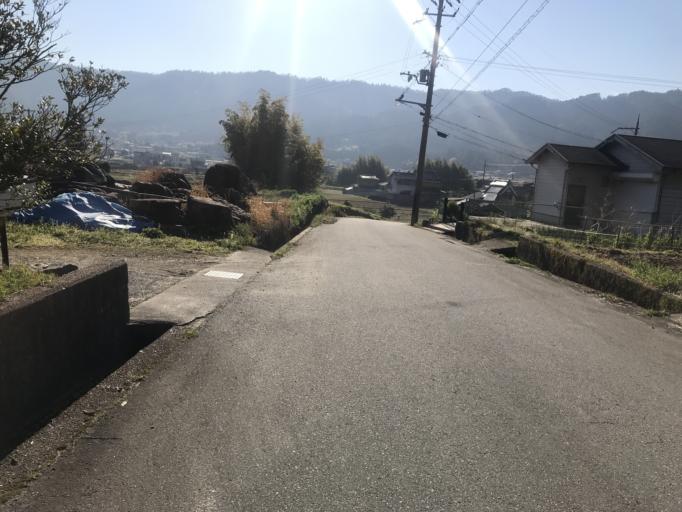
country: JP
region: Kyoto
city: Kameoka
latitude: 34.9857
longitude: 135.5394
